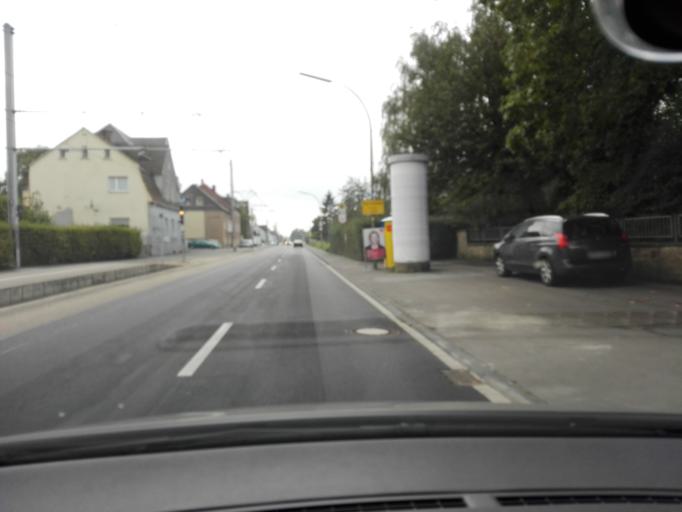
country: DE
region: North Rhine-Westphalia
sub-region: Regierungsbezirk Arnsberg
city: Holzwickede
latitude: 51.5302
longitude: 7.6010
